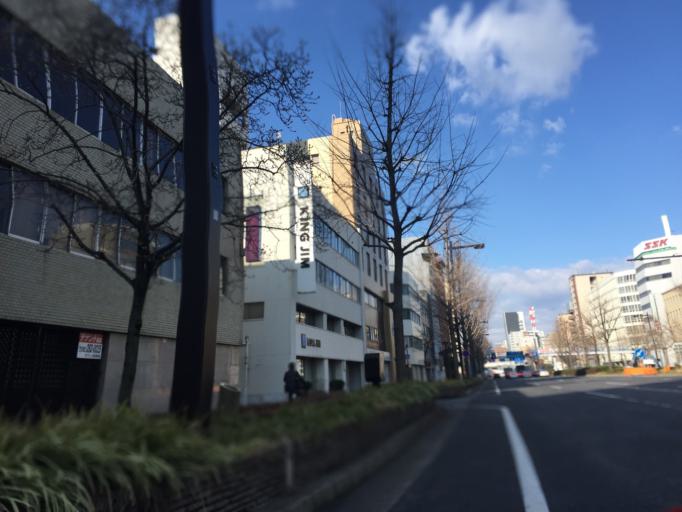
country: JP
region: Aichi
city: Nagoya-shi
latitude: 35.1740
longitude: 136.9233
